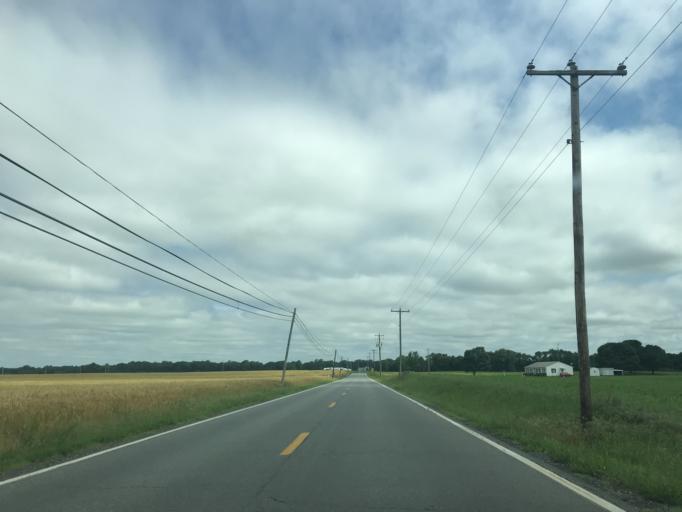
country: US
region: Maryland
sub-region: Caroline County
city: Ridgely
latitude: 38.9019
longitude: -75.9587
